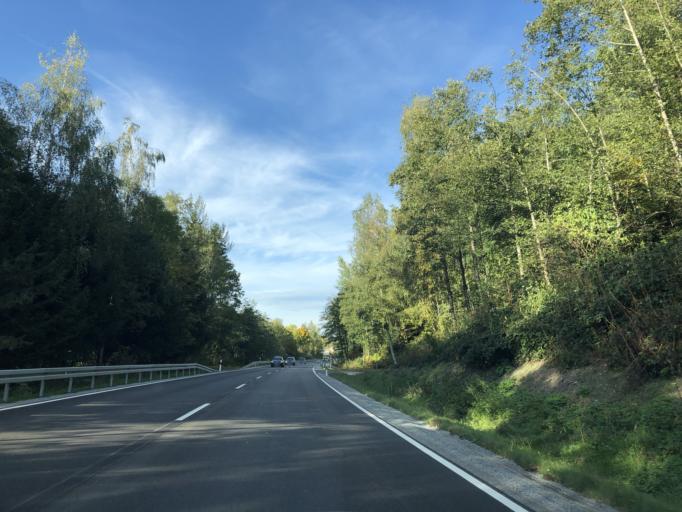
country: DE
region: Bavaria
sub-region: Lower Bavaria
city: Grafling
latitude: 48.9055
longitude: 12.9776
